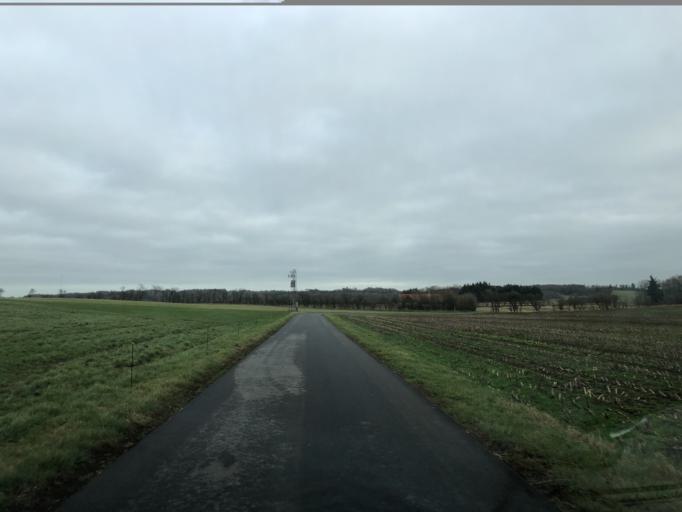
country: DK
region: Central Jutland
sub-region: Viborg Kommune
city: Stoholm
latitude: 56.4506
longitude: 9.1199
